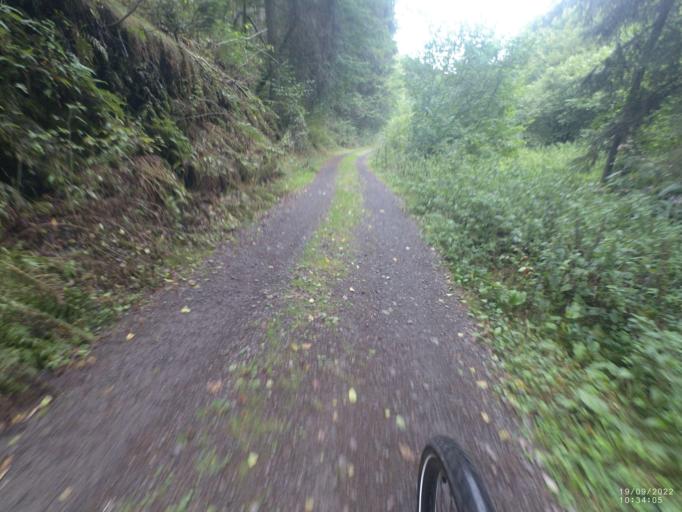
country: DE
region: Rheinland-Pfalz
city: Meerfeld
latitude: 50.1113
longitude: 6.7513
